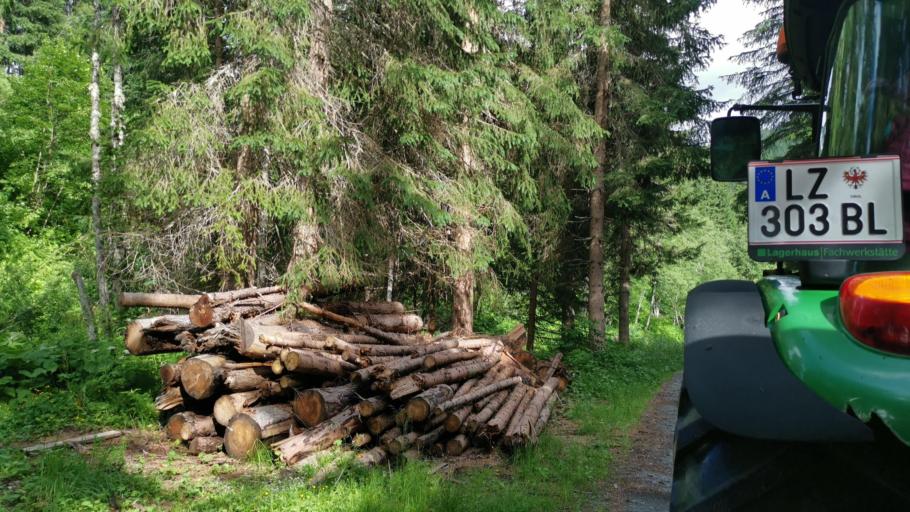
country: AT
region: Tyrol
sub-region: Politischer Bezirk Lienz
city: Obertilliach
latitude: 46.7030
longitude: 12.6044
